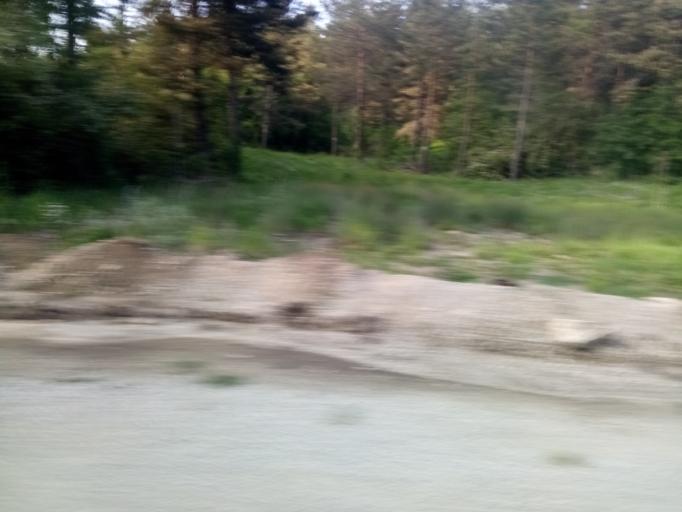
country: TR
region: Karabuk
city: Eskipazar
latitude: 41.0509
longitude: 32.5421
